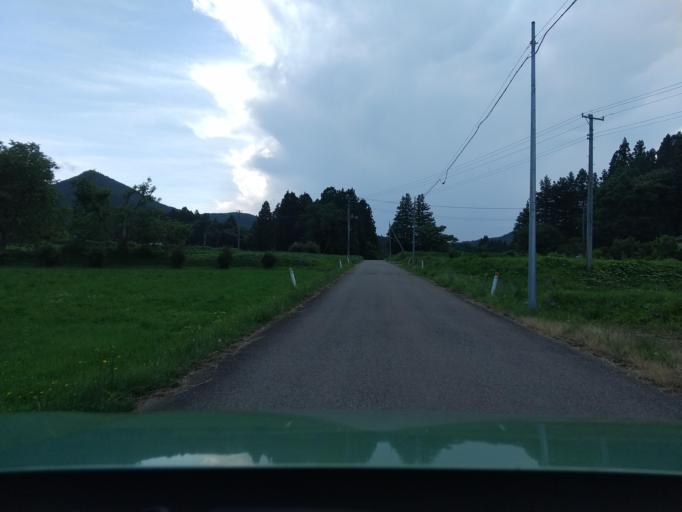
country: JP
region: Iwate
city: Ichinoseki
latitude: 39.0045
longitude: 141.2206
